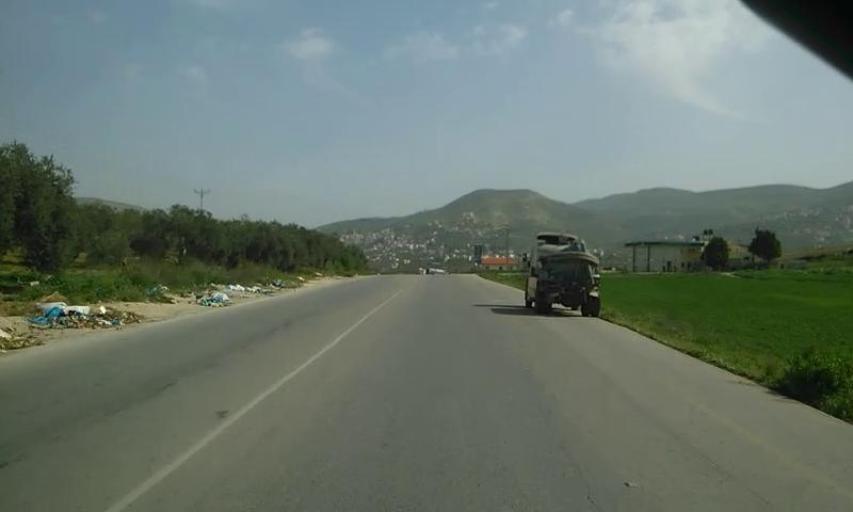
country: PS
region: West Bank
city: Al Fandaqumiyah
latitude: 32.3392
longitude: 35.2041
